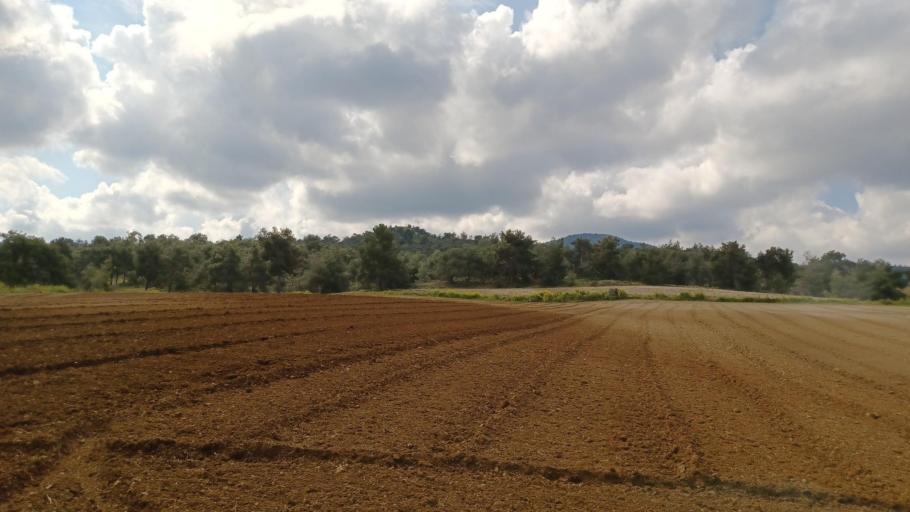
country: CY
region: Lefkosia
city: Kakopetria
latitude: 35.0758
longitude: 32.9567
